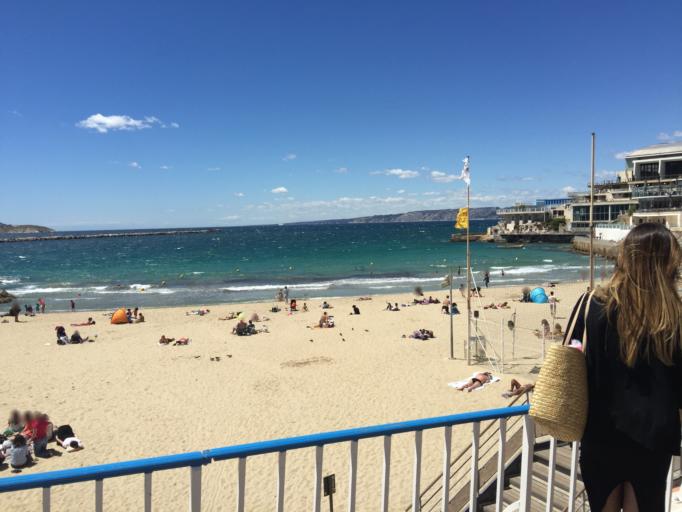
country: FR
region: Provence-Alpes-Cote d'Azur
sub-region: Departement des Bouches-du-Rhone
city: Marseille 07
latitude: 43.2904
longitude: 5.3559
